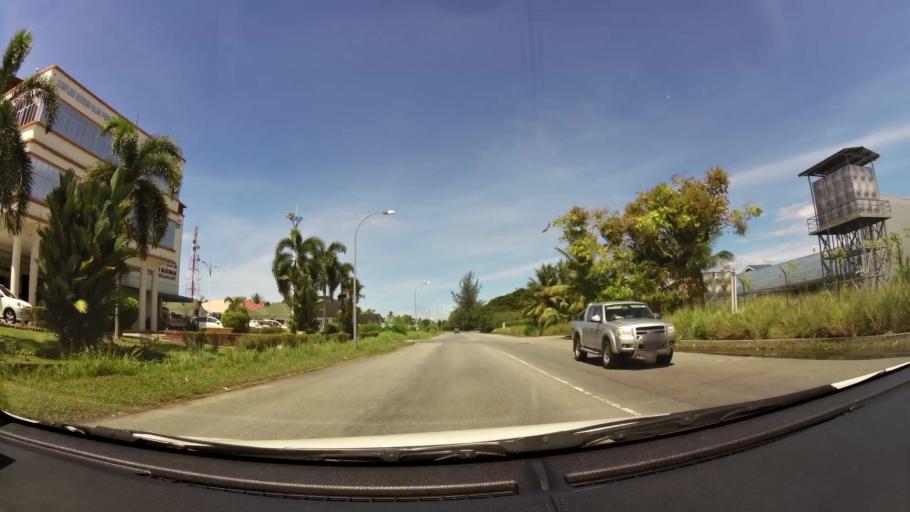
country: BN
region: Belait
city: Kuala Belait
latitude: 4.5893
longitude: 114.2293
